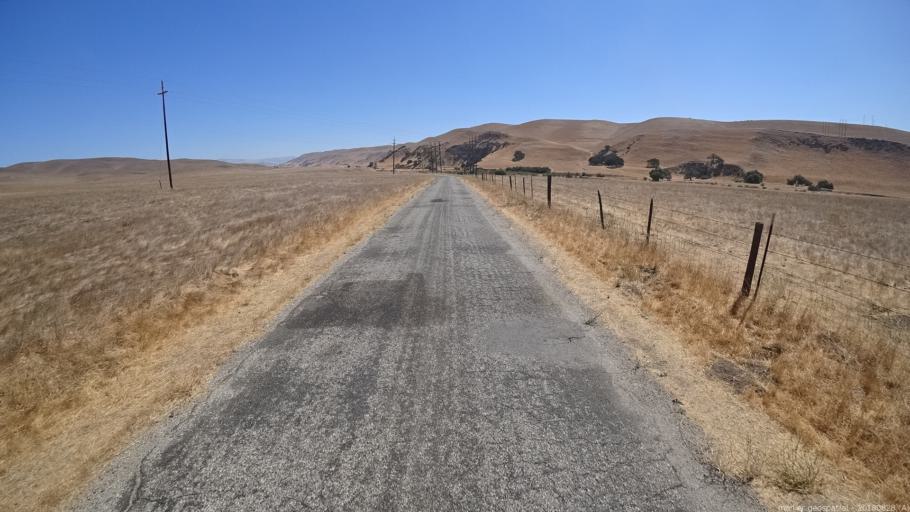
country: US
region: California
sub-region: San Luis Obispo County
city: Lake Nacimiento
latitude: 36.0234
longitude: -120.8805
